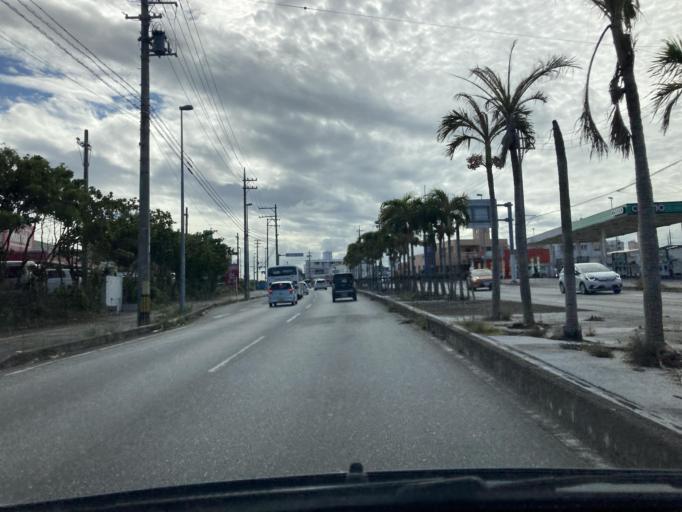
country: JP
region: Okinawa
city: Tomigusuku
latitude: 26.1637
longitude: 127.7243
